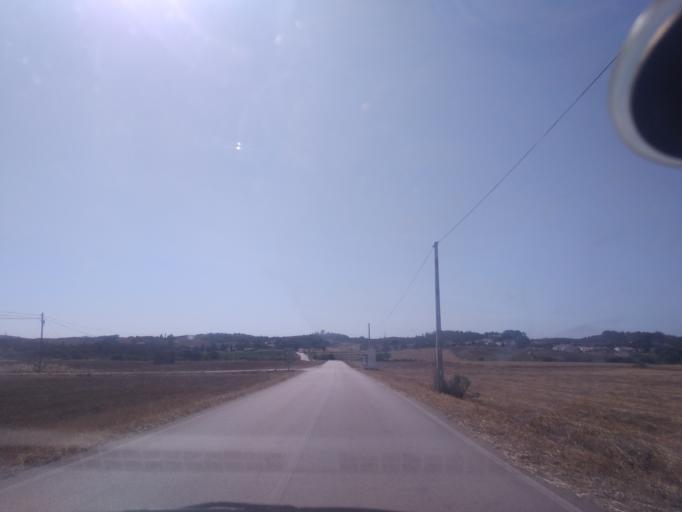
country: PT
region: Faro
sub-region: Aljezur
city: Aljezur
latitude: 37.2281
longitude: -8.8245
